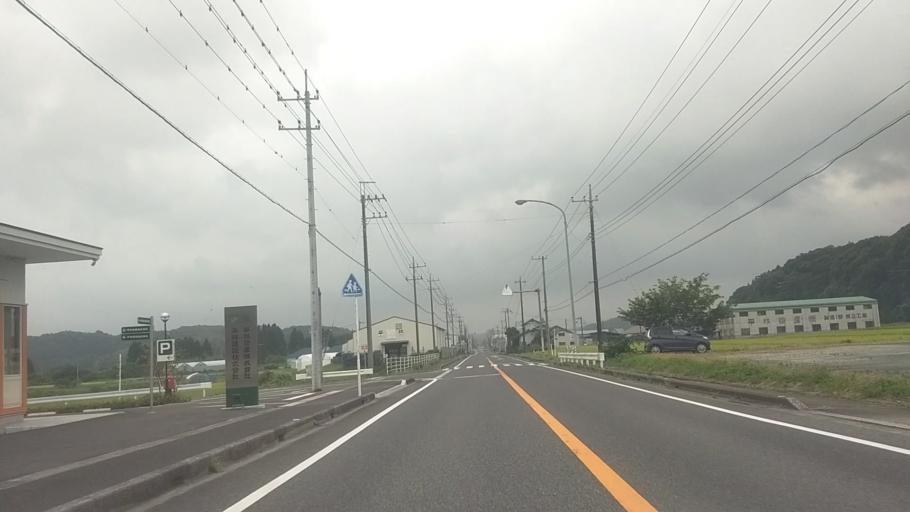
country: JP
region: Chiba
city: Ohara
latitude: 35.2877
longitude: 140.2580
